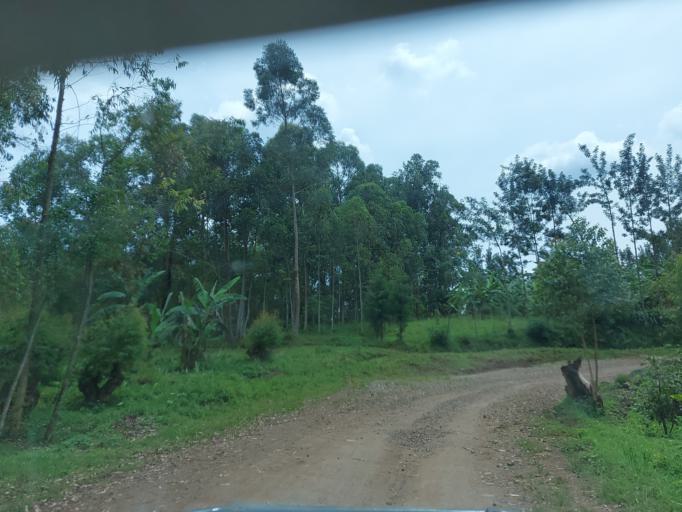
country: CD
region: South Kivu
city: Bukavu
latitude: -2.2457
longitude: 28.8215
